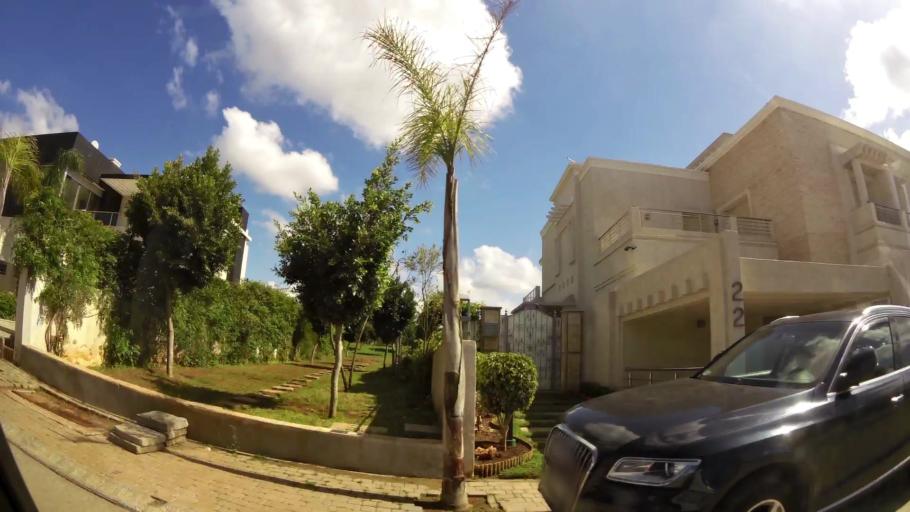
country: MA
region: Grand Casablanca
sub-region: Nouaceur
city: Bouskoura
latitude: 33.4677
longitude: -7.6054
